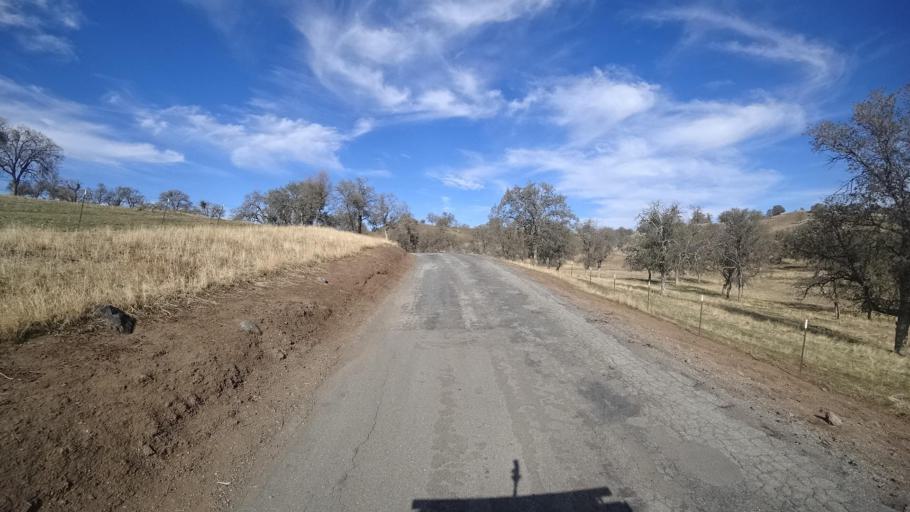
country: US
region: California
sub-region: Kern County
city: Oildale
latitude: 35.6026
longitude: -118.8253
